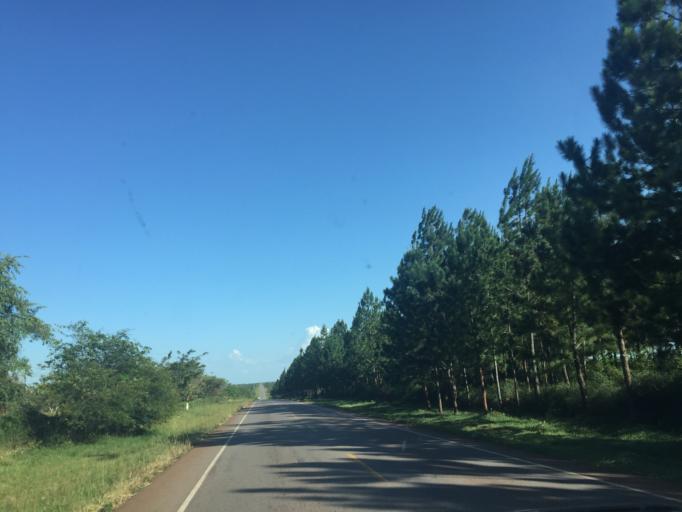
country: UG
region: Central Region
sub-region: Nakasongola District
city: Nakasongola
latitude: 1.3752
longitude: 32.3467
